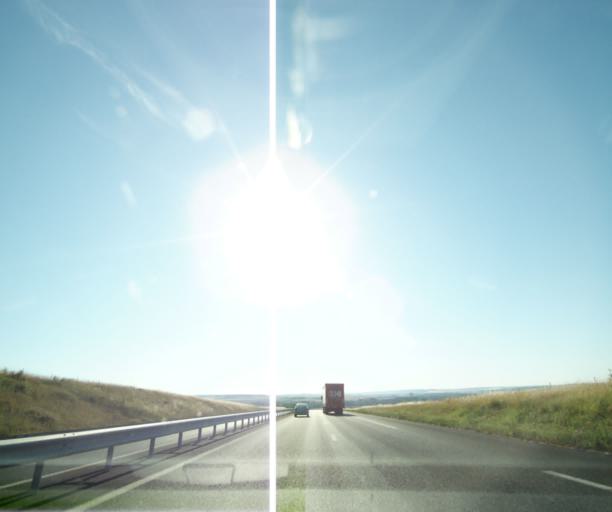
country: FR
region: Bourgogne
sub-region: Departement de l'Yonne
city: Thorigny-sur-Oreuse
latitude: 48.2446
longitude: 3.5057
